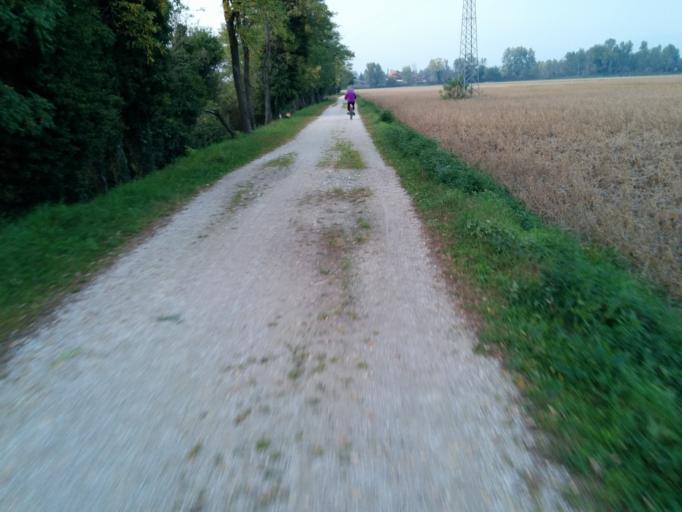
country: IT
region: Friuli Venezia Giulia
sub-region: Provincia di Udine
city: Povoletto
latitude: 46.1029
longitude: 13.2743
